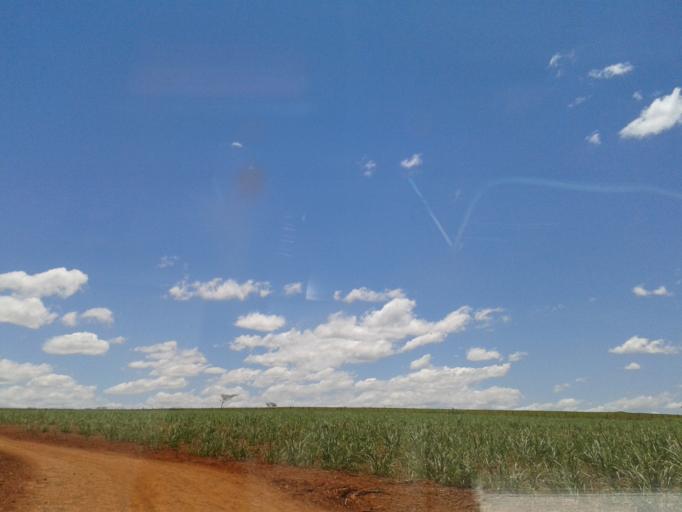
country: BR
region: Minas Gerais
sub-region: Centralina
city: Centralina
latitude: -18.6671
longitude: -49.2328
